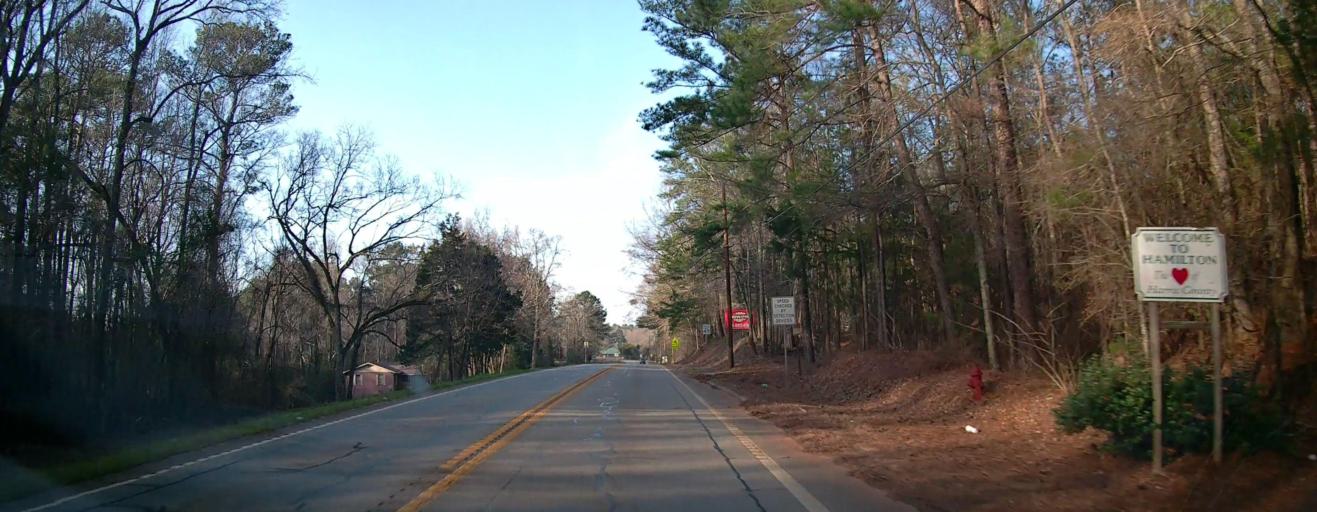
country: US
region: Georgia
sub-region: Harris County
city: Hamilton
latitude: 32.7457
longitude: -84.8699
